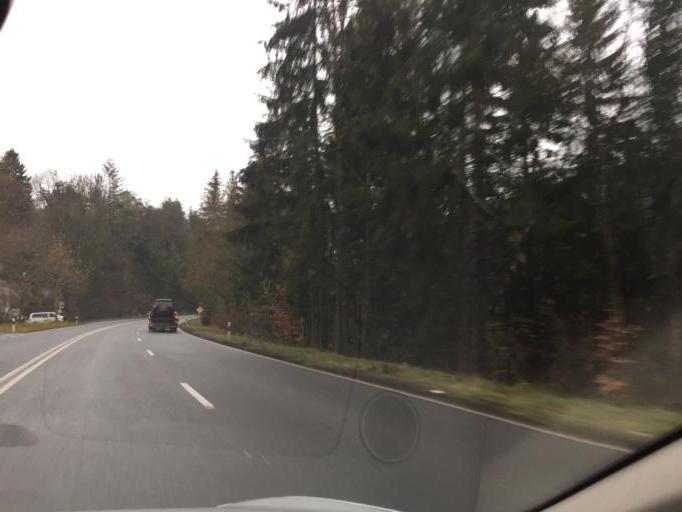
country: LU
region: Diekirch
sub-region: Canton de Diekirch
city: Diekirch
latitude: 49.8790
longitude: 6.1521
